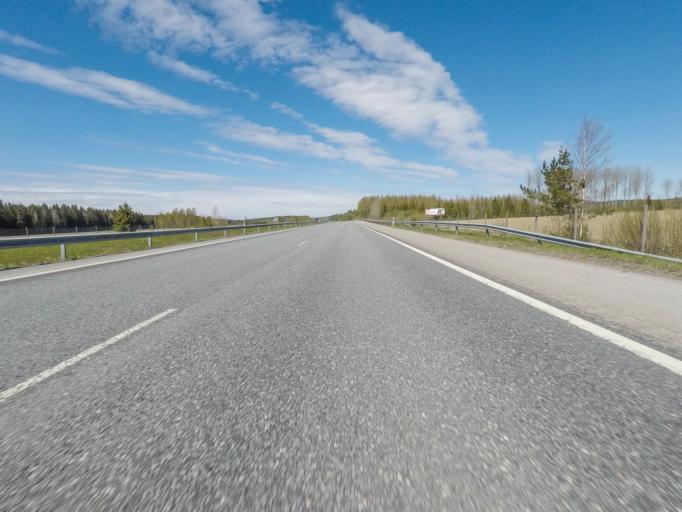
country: FI
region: Haeme
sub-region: Riihimaeki
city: Riihimaeki
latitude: 60.7716
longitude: 24.7161
